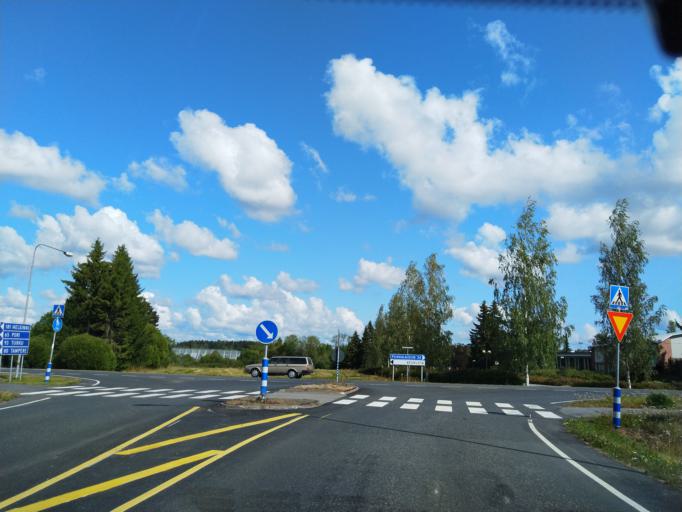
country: FI
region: Satakunta
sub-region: Pori
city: Huittinen
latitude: 61.1788
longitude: 22.7129
